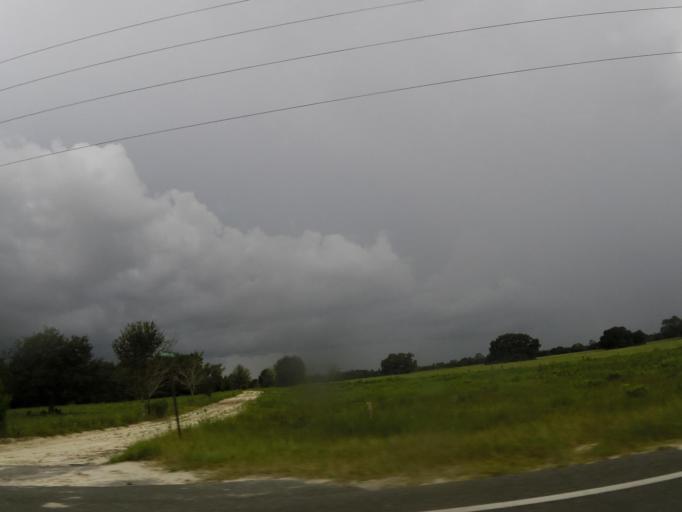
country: US
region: Florida
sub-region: Baker County
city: Macclenny
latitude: 30.3869
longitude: -82.1763
